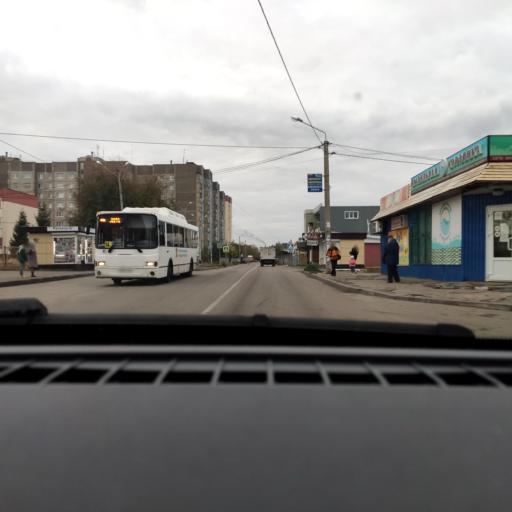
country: RU
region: Voronezj
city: Somovo
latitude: 51.7366
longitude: 39.2913
